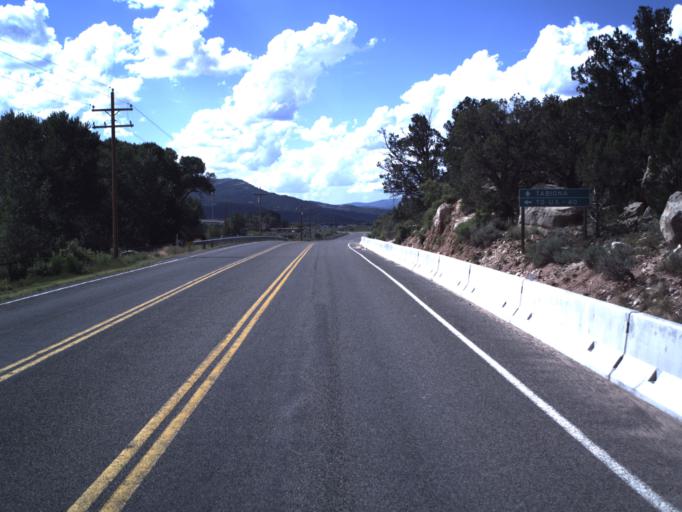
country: US
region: Utah
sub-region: Duchesne County
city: Duchesne
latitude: 40.3300
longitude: -110.6691
